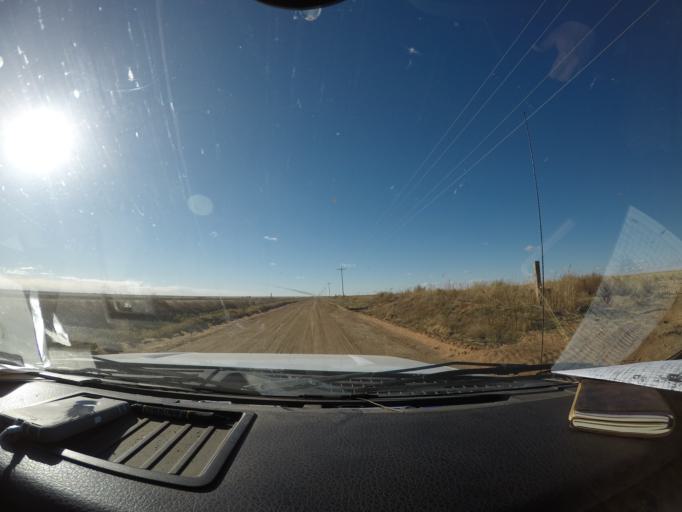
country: US
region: New Mexico
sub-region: Curry County
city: Clovis
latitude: 34.5649
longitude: -103.2595
